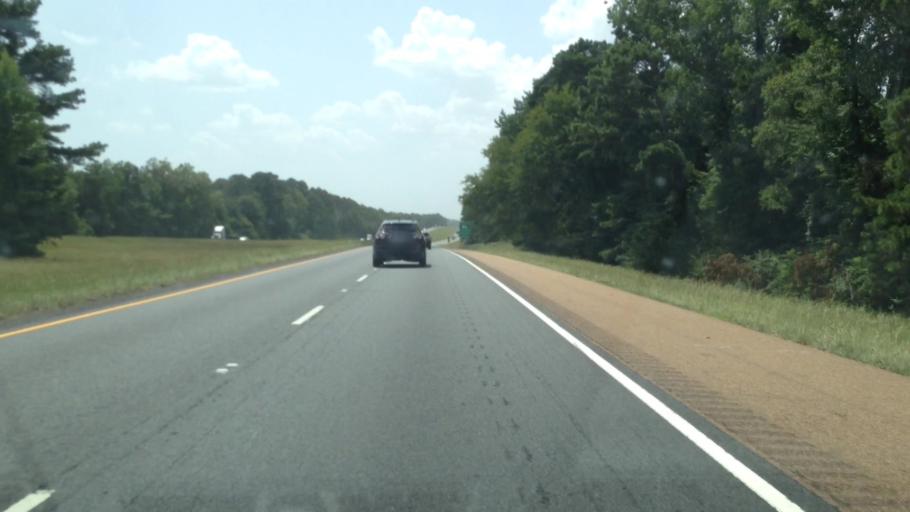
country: US
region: Louisiana
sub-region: Bienville Parish
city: Arcadia
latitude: 32.5588
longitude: -92.8861
